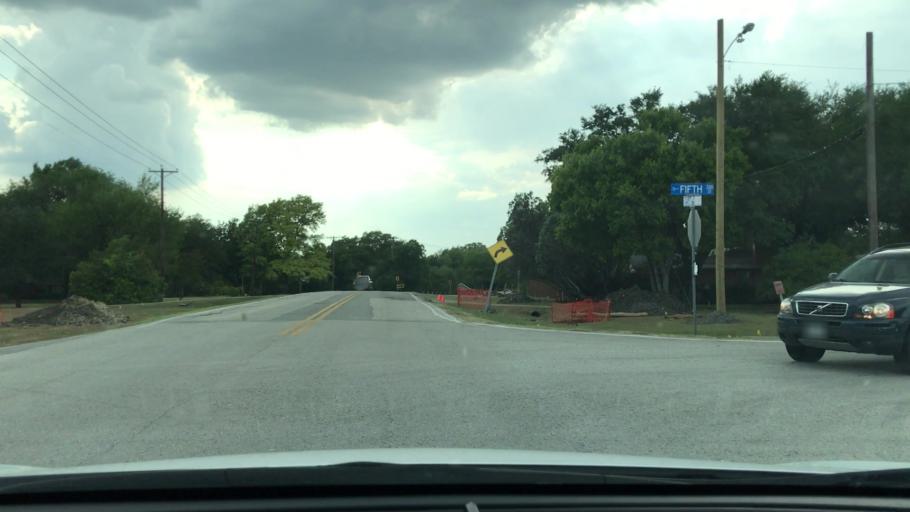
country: US
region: Texas
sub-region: Dallas County
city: Sachse
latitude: 32.9733
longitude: -96.5916
